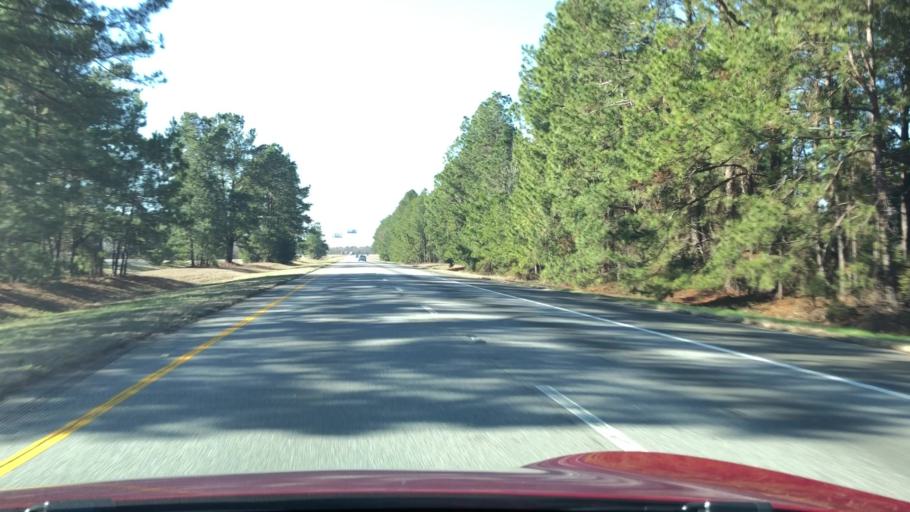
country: US
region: South Carolina
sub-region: Clarendon County
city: Manning
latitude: 33.6061
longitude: -80.3215
